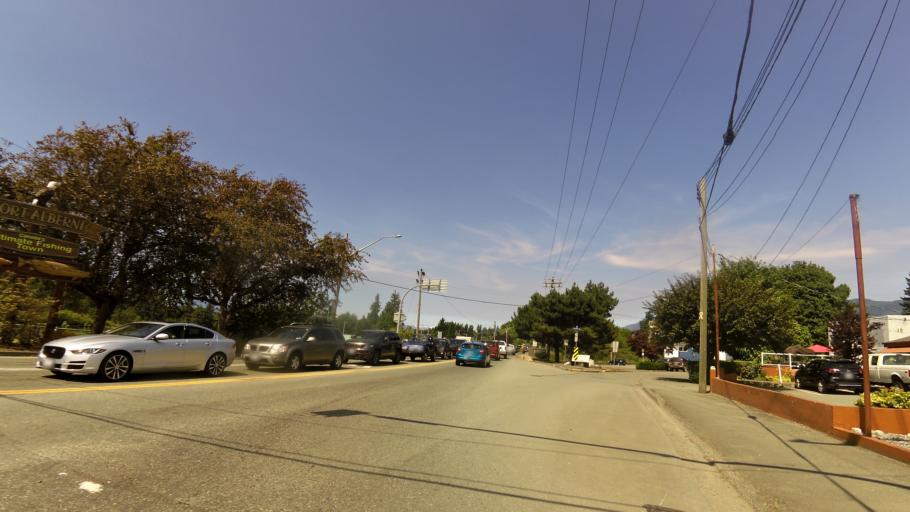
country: CA
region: British Columbia
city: Port Alberni
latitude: 49.2576
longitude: -124.8136
